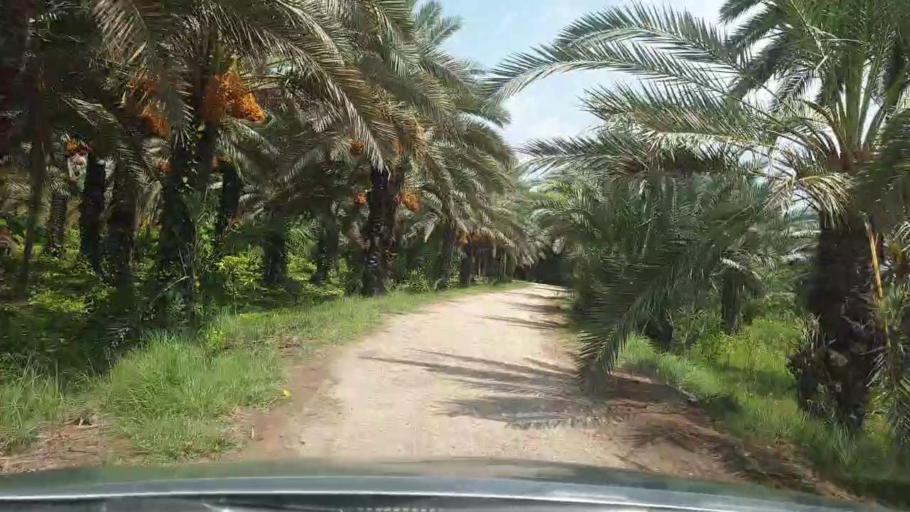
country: PK
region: Sindh
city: Pir jo Goth
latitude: 27.6154
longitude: 68.6664
